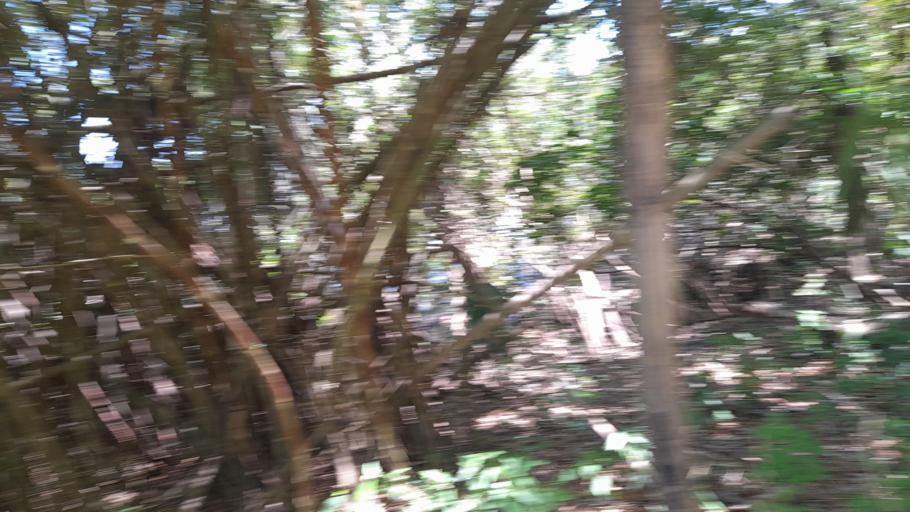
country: PE
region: Ucayali
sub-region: Provincia de Coronel Portillo
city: Puerto Callao
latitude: -8.2609
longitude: -74.6404
